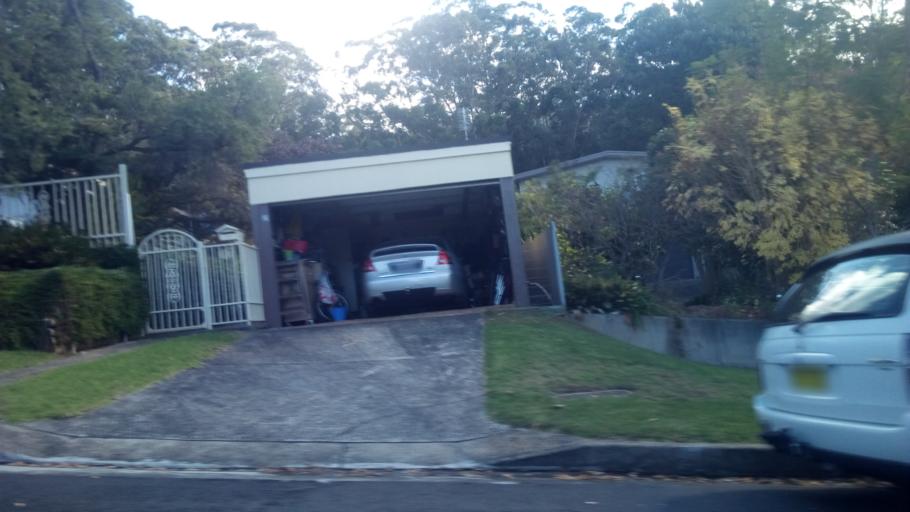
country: AU
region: New South Wales
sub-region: Wollongong
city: Cordeaux Heights
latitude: -34.4305
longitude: 150.8176
